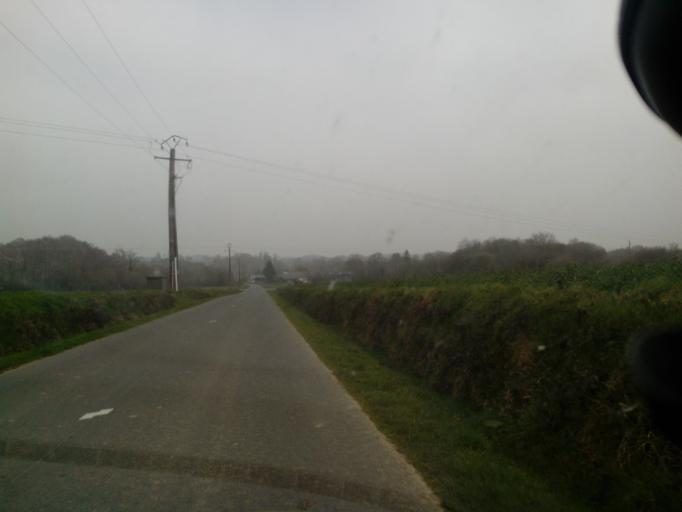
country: FR
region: Brittany
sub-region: Departement d'Ille-et-Vilaine
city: Gael
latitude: 48.1710
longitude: -2.2532
